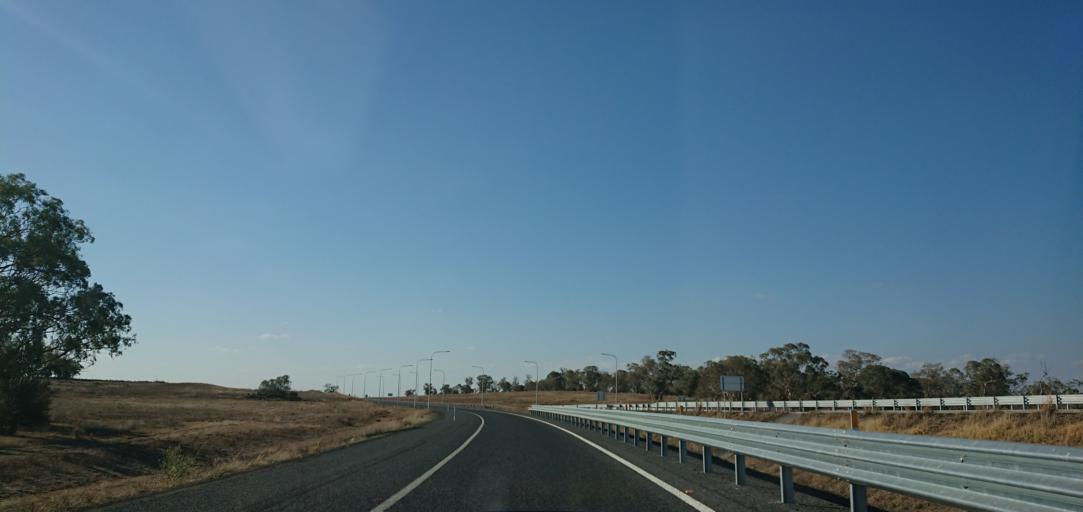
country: AU
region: Queensland
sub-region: Toowoomba
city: Westbrook
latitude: -27.6120
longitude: 151.7863
